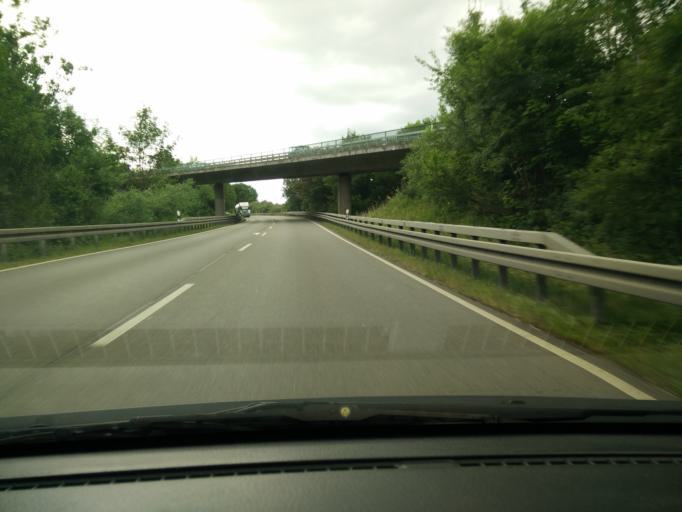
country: DE
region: Baden-Wuerttemberg
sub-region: Freiburg Region
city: Bad Durrheim
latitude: 48.0391
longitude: 8.5337
